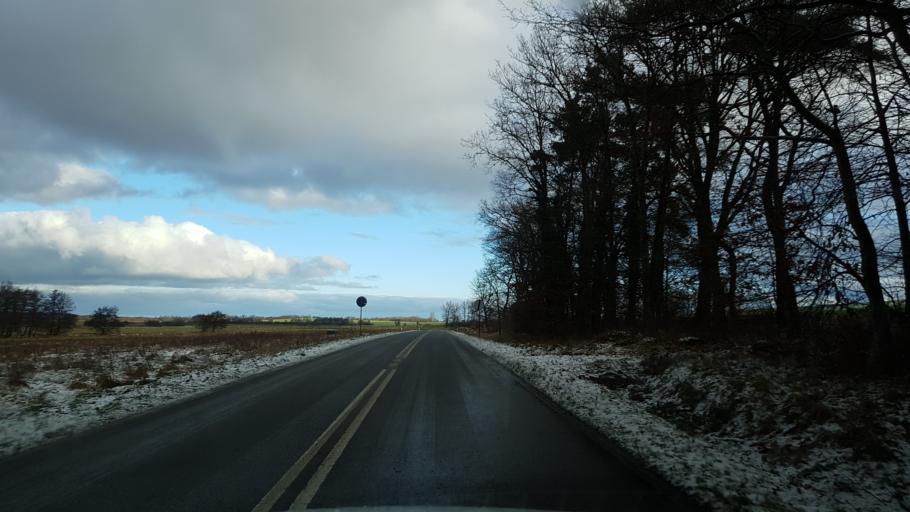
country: PL
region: West Pomeranian Voivodeship
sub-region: Powiat gryficki
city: Karnice
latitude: 54.0451
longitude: 15.0619
